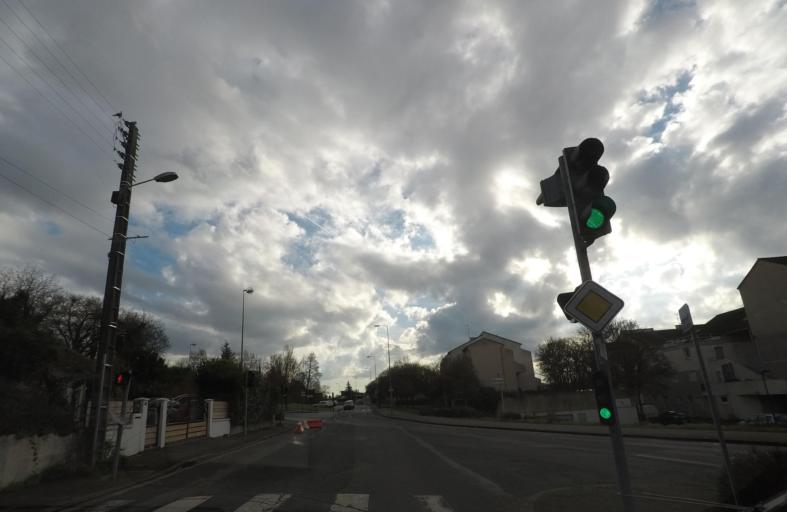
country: FR
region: Centre
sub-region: Departement du Cher
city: Bourges
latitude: 47.0608
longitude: 2.4011
